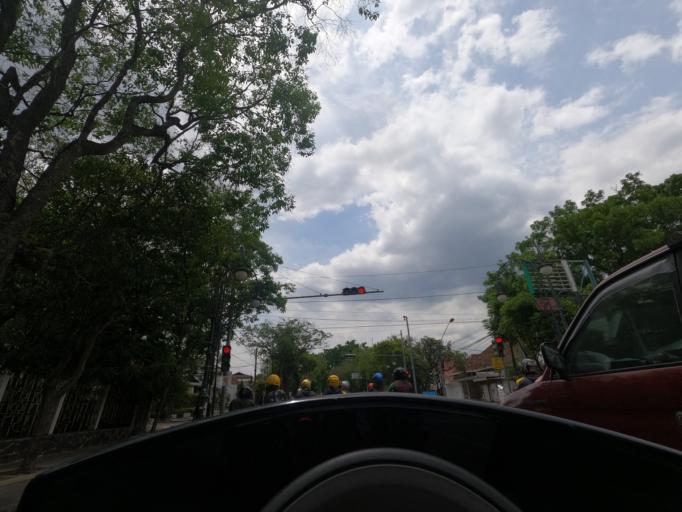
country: ID
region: West Java
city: Bandung
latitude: -6.9129
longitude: 107.6287
